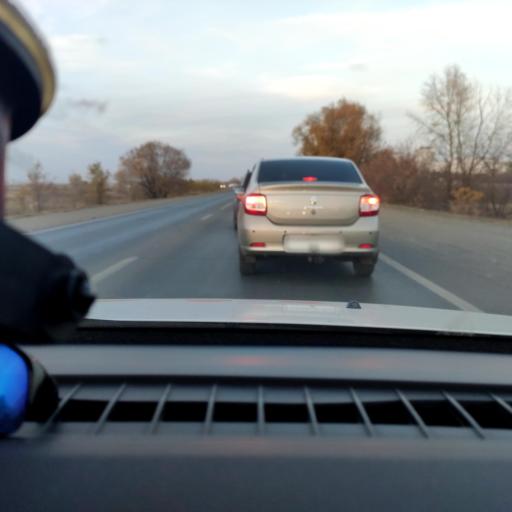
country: RU
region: Samara
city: Samara
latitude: 53.0893
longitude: 50.1477
